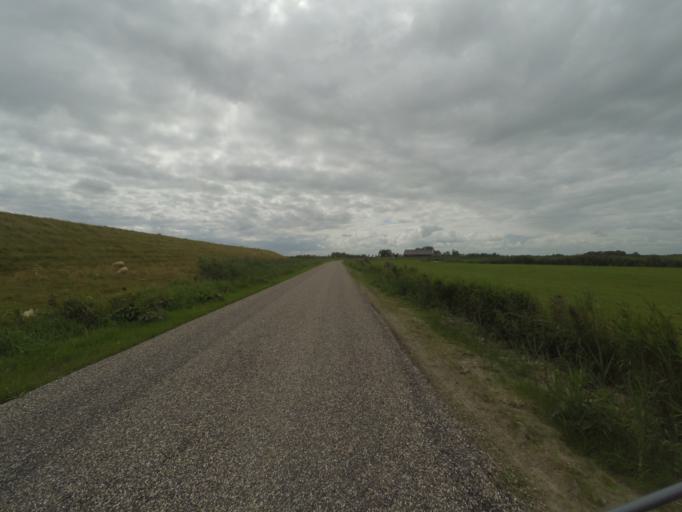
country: NL
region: Friesland
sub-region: Gemeente Dongeradeel
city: Anjum
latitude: 53.3540
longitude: 6.1436
